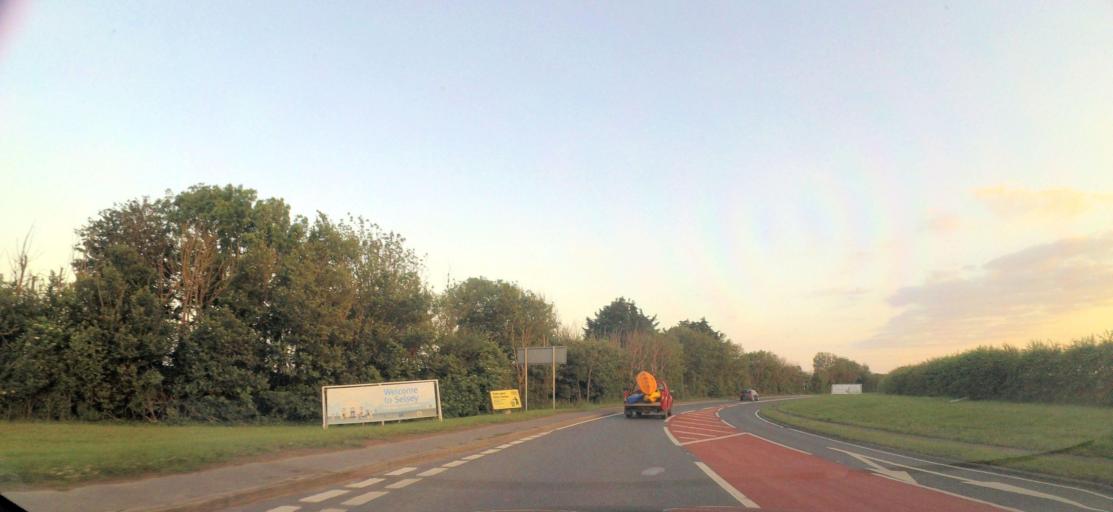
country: GB
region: England
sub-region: West Sussex
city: Selsey
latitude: 50.7458
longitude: -0.7787
